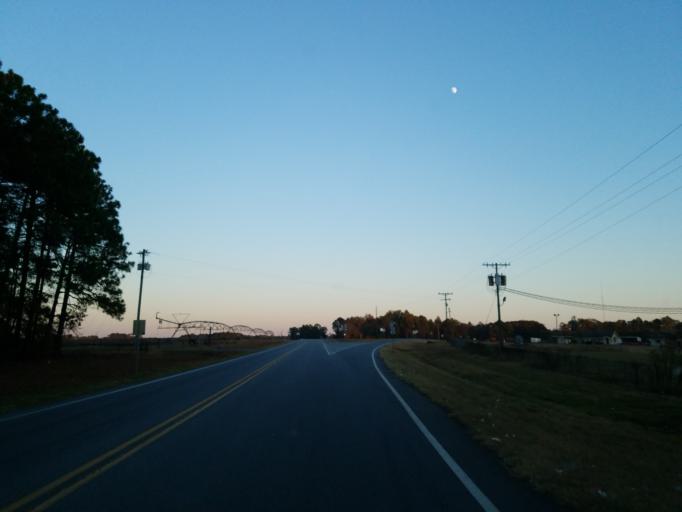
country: US
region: Georgia
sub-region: Irwin County
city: Ocilla
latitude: 31.6457
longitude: -83.3526
